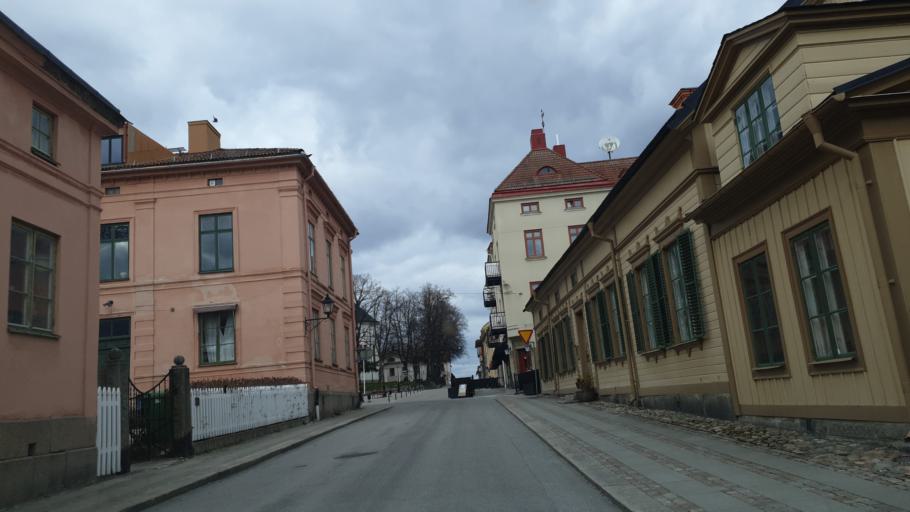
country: SE
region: OErebro
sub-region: Nora Kommun
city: Nora
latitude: 59.5182
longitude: 15.0412
